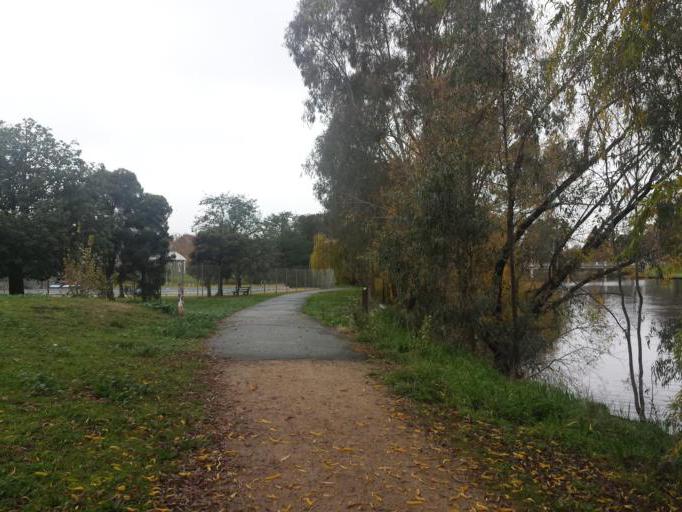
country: AU
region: Victoria
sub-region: Benalla
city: Benalla
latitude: -36.5507
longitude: 145.9797
